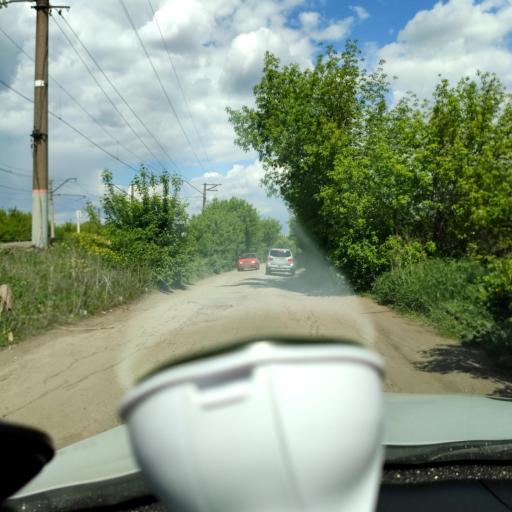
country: RU
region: Samara
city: Petra-Dubrava
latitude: 53.2732
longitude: 50.3181
